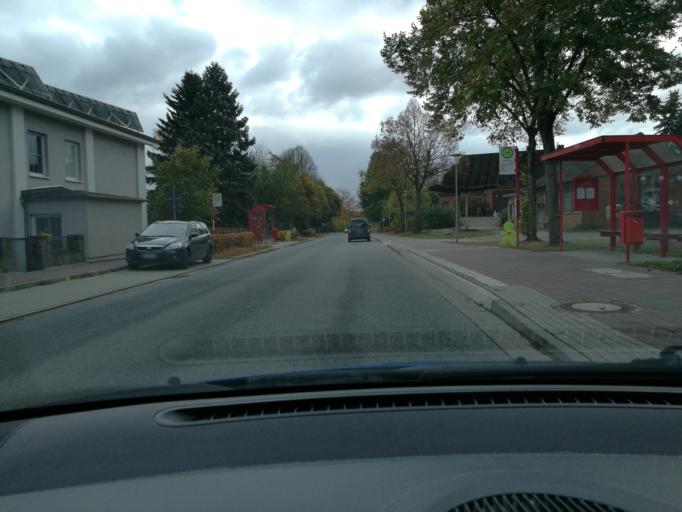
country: DE
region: Schleswig-Holstein
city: Pogeez
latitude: 53.7503
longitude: 10.7287
